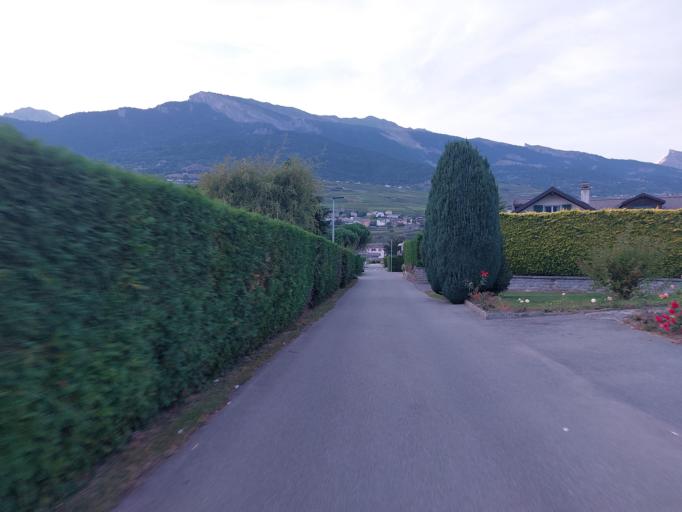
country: CH
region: Valais
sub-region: Conthey District
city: Conthey
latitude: 46.2261
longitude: 7.3072
